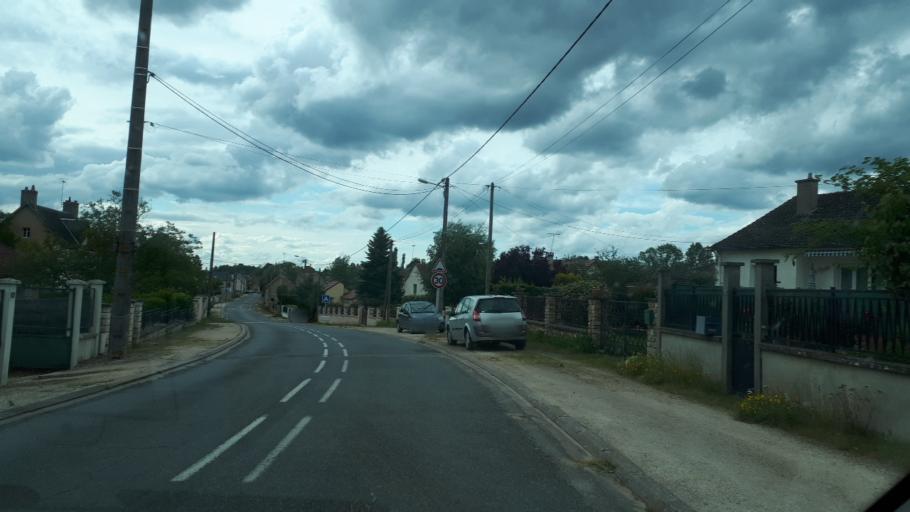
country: FR
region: Centre
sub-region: Departement du Cher
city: Gracay
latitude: 47.1415
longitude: 1.8557
